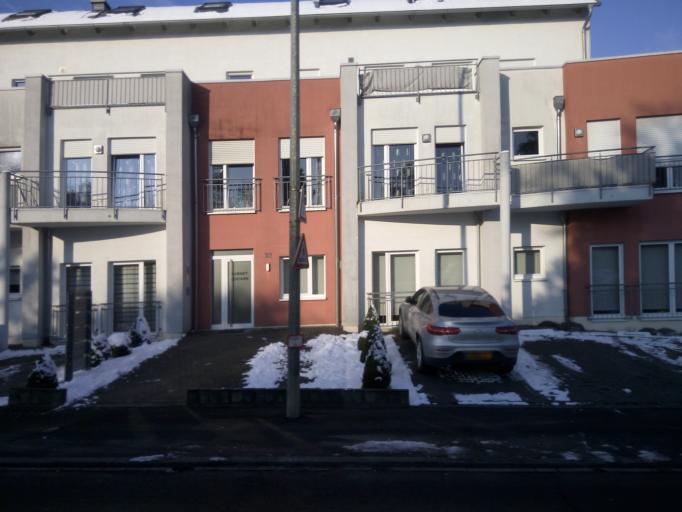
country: LU
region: Grevenmacher
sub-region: Canton de Grevenmacher
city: Junglinster
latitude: 49.7092
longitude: 6.2502
